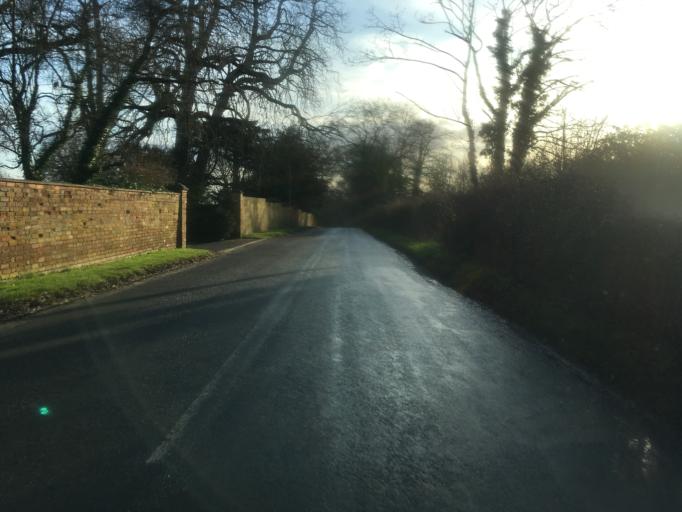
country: GB
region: England
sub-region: Warwickshire
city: Stratford-upon-Avon
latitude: 52.2273
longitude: -1.6892
